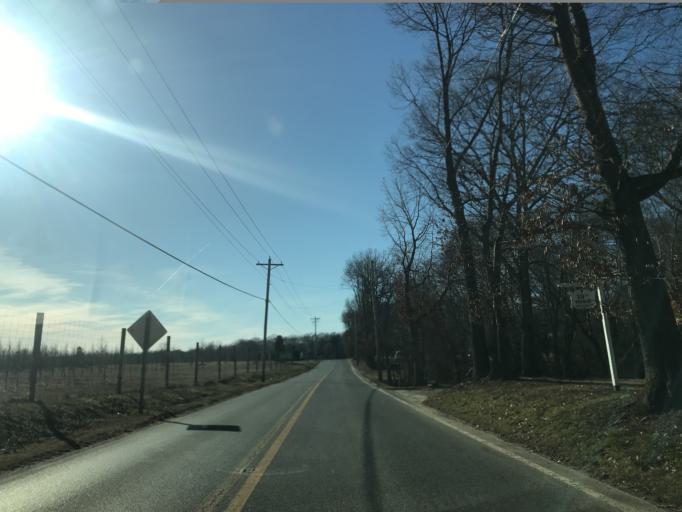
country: US
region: Maryland
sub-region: Prince George's County
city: Accokeek
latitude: 38.6703
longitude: -76.9800
